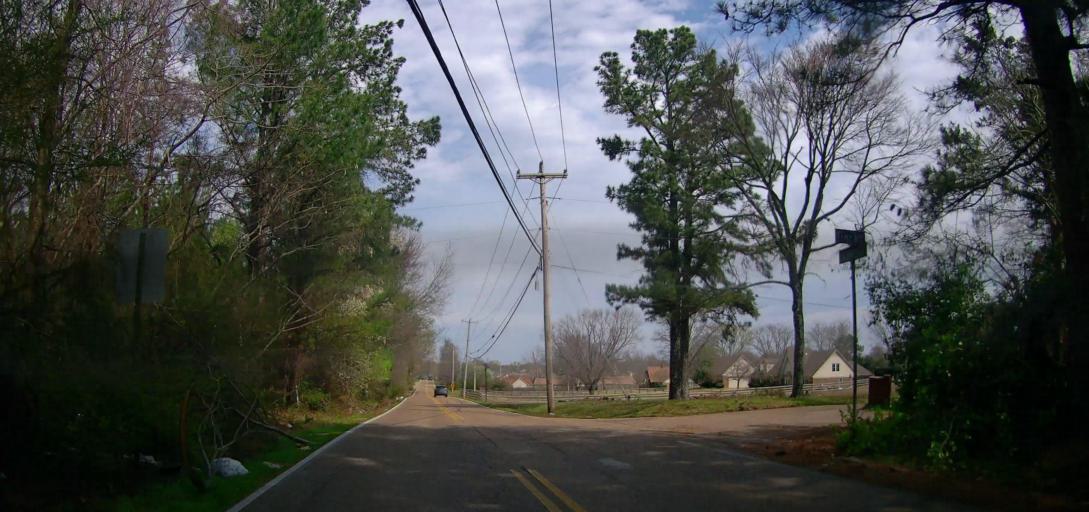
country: US
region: Mississippi
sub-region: De Soto County
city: Olive Branch
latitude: 34.9985
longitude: -89.8484
